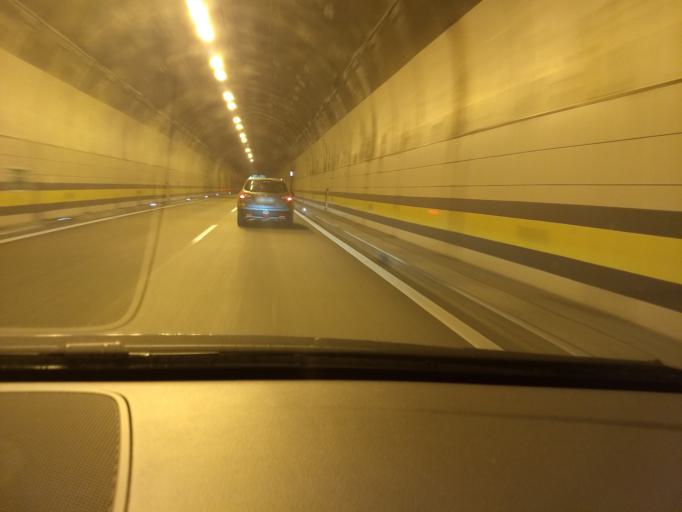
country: CH
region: Uri
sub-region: Uri
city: Silenen
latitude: 46.7665
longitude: 8.6637
